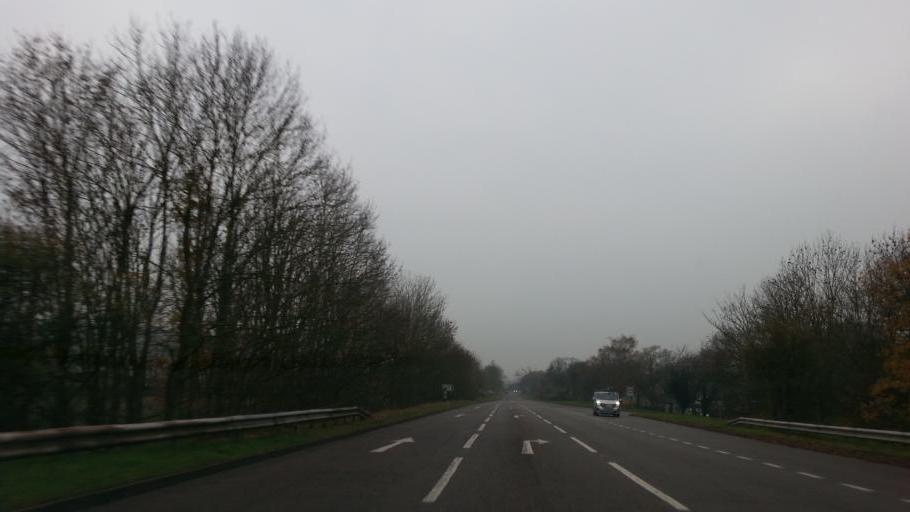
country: GB
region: England
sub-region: Peterborough
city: Castor
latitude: 52.5453
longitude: -0.3350
